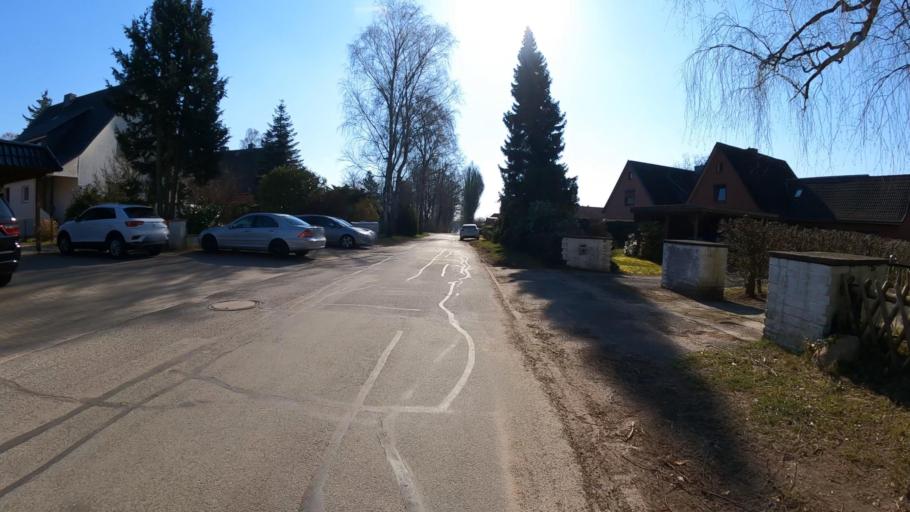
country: DE
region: Lower Saxony
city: Bendestorf
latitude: 53.3508
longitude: 9.9207
